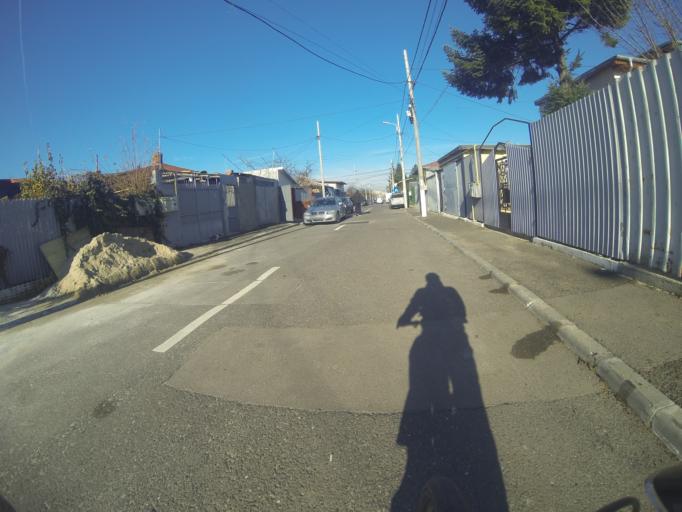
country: RO
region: Bucuresti
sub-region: Municipiul Bucuresti
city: Bucuresti
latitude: 44.3965
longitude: 26.0657
